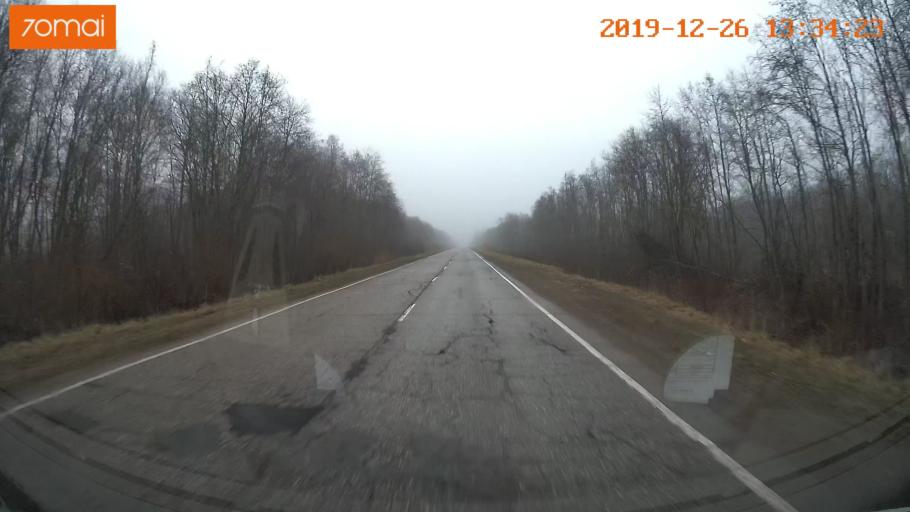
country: RU
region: Vologda
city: Sheksna
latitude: 58.8062
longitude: 38.3228
